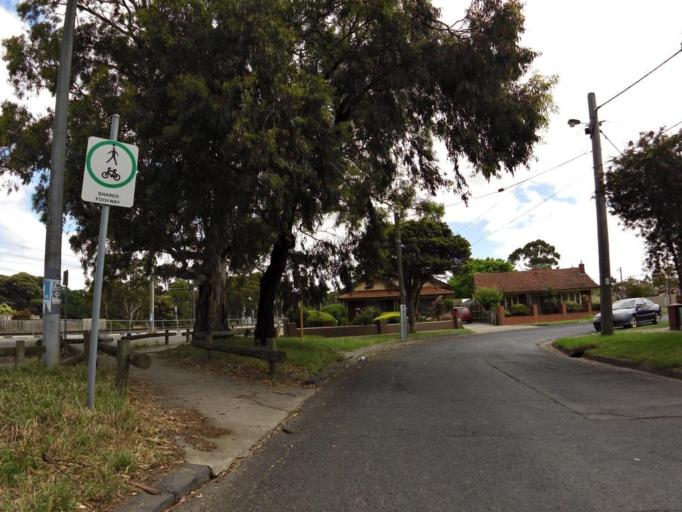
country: AU
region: Victoria
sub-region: Moreland
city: Fawkner
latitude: -37.7204
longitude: 144.9616
